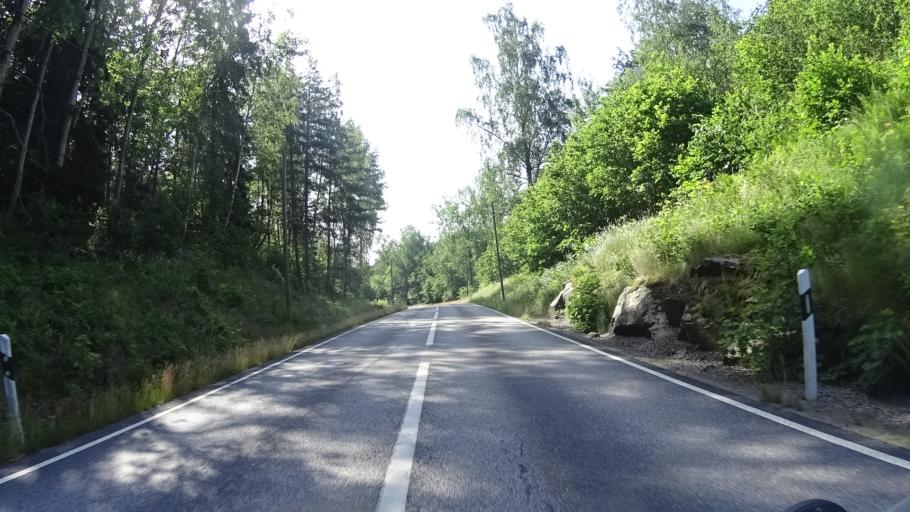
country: SE
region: Kalmar
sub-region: Vasterviks Kommun
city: Overum
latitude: 58.0212
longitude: 16.2430
